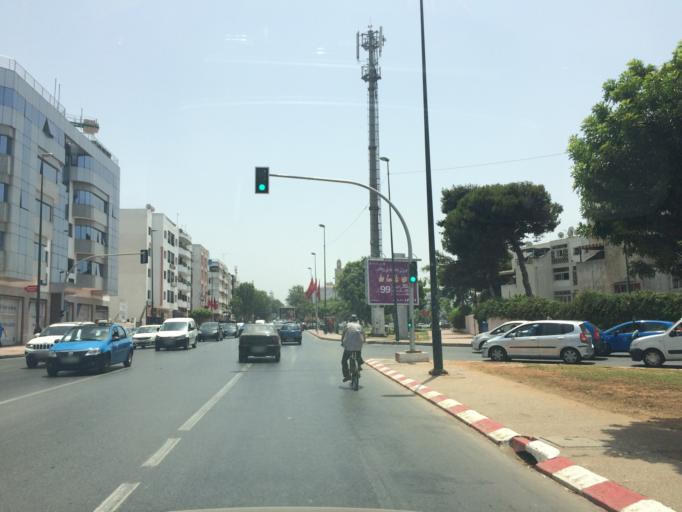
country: MA
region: Rabat-Sale-Zemmour-Zaer
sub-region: Rabat
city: Rabat
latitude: 34.0039
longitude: -6.8518
